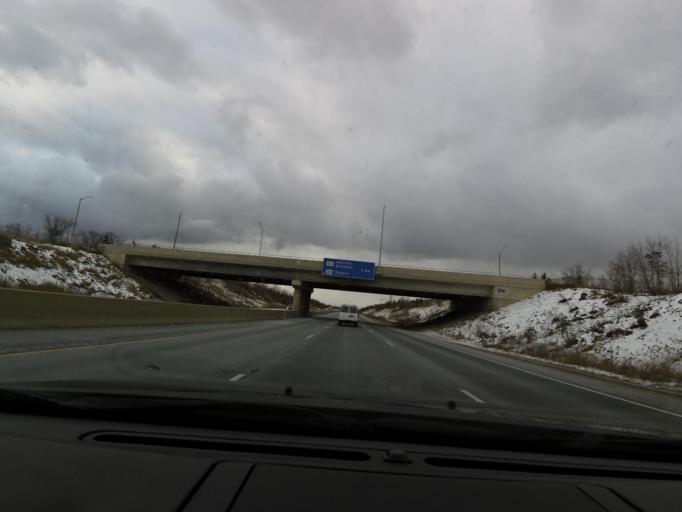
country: CA
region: Ontario
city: Burlington
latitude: 43.3599
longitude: -79.8320
